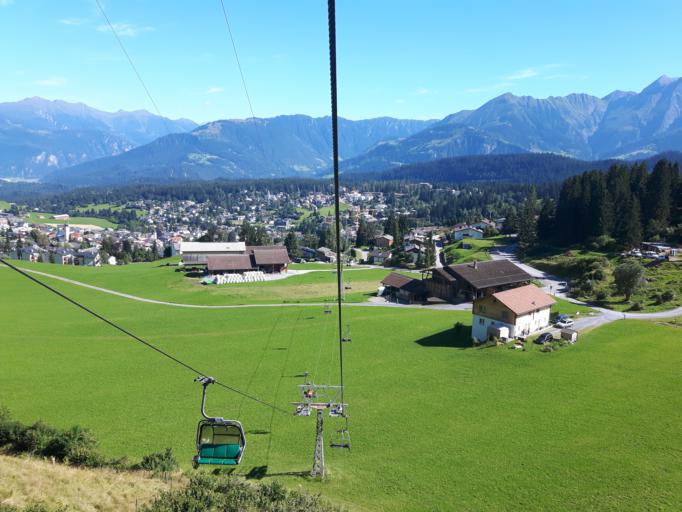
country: CH
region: Grisons
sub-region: Imboden District
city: Flims
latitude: 46.8412
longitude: 9.2735
